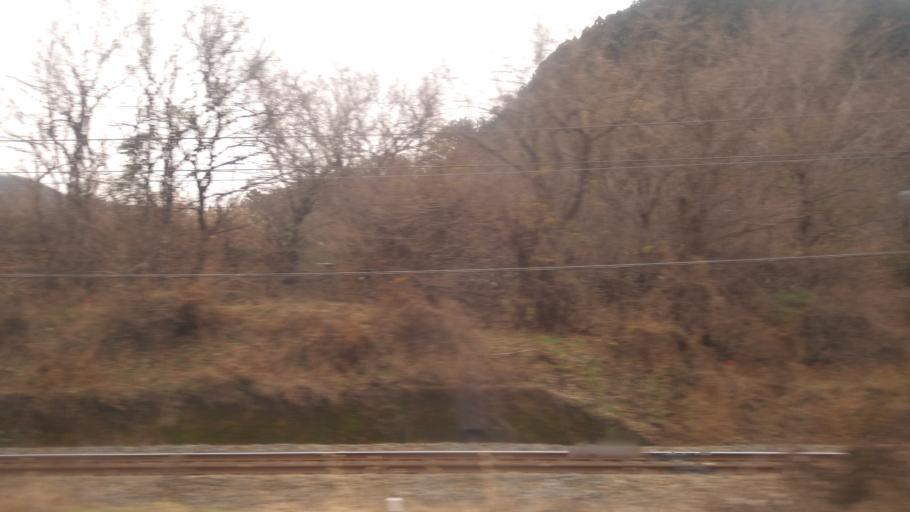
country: JP
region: Nagano
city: Ina
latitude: 35.8980
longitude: 137.7681
